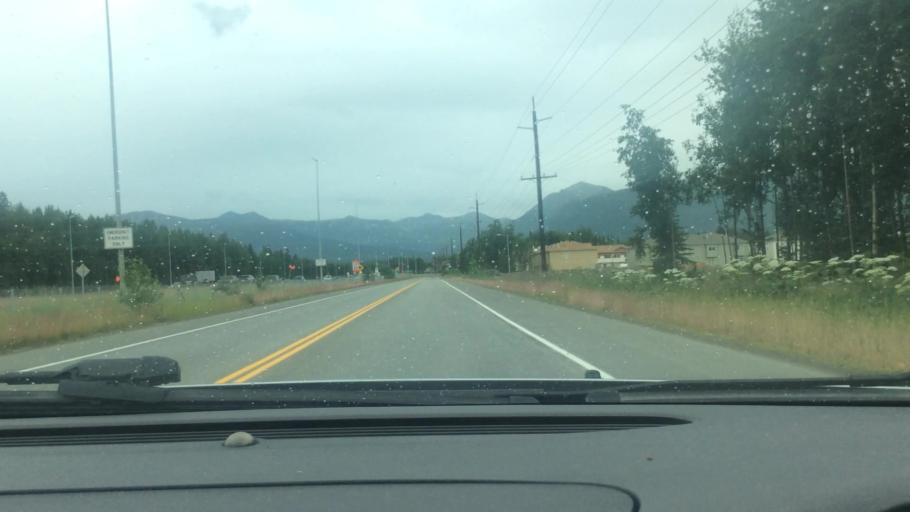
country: US
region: Alaska
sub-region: Anchorage Municipality
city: Anchorage
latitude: 61.2242
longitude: -149.7671
